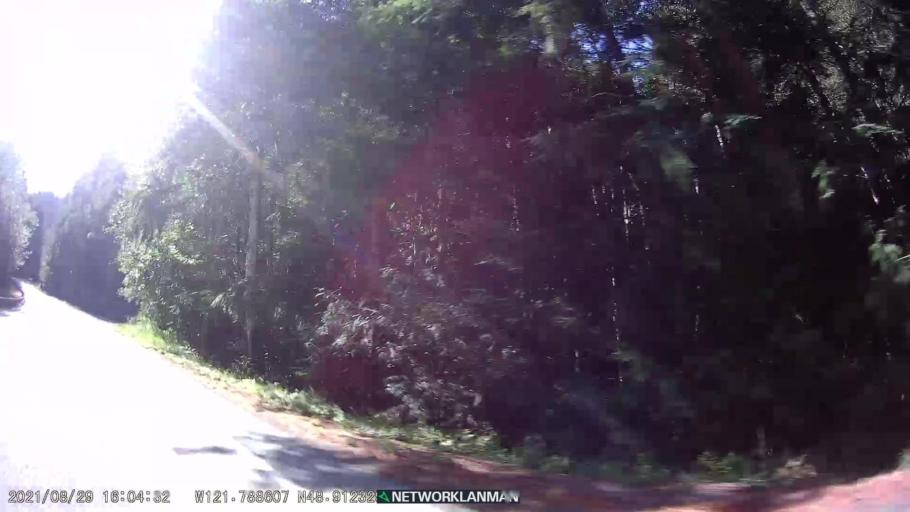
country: CA
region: British Columbia
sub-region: Fraser Valley Regional District
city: Chilliwack
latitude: 48.9123
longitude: -121.7889
